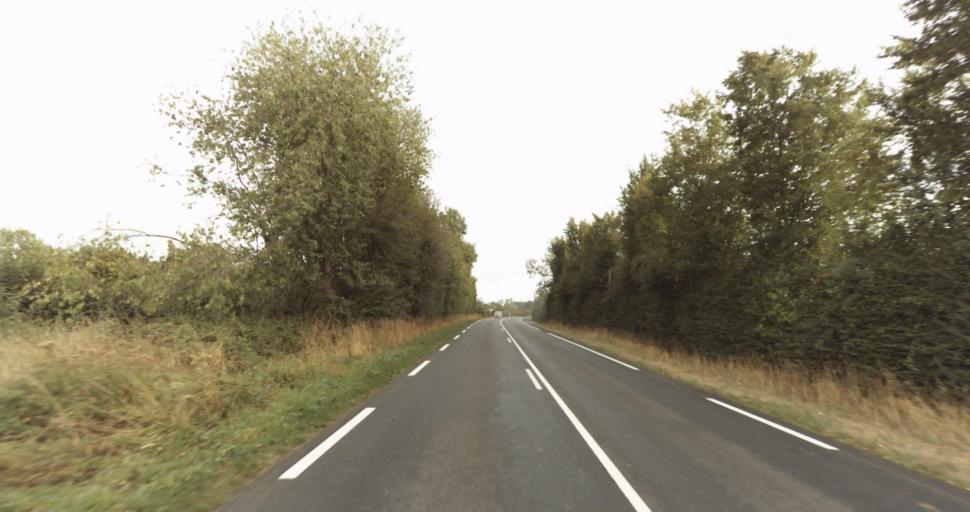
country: FR
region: Lower Normandy
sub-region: Departement de l'Orne
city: Vimoutiers
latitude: 48.8784
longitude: 0.2561
